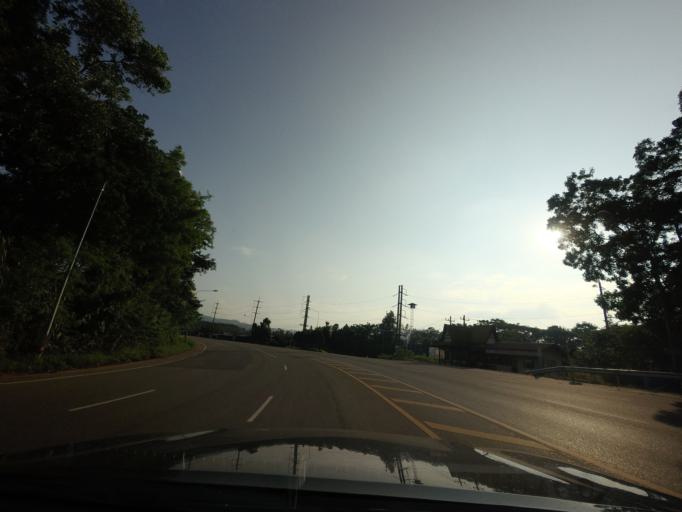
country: TH
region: Loei
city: Dan Sai
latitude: 17.2062
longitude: 101.1596
